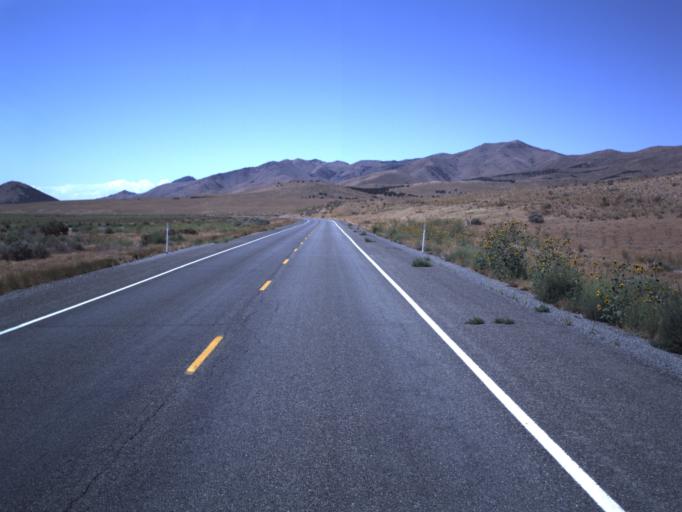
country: US
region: Utah
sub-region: Juab County
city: Nephi
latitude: 39.6340
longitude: -112.1084
